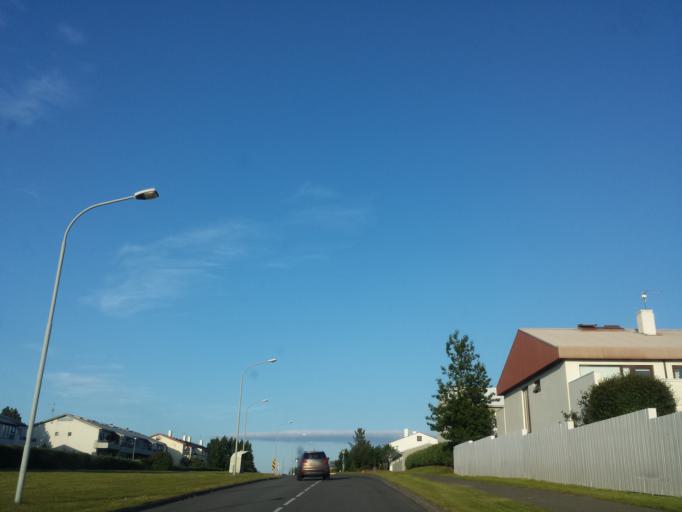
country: IS
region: Capital Region
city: Reykjavik
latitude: 64.1212
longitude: -21.8187
